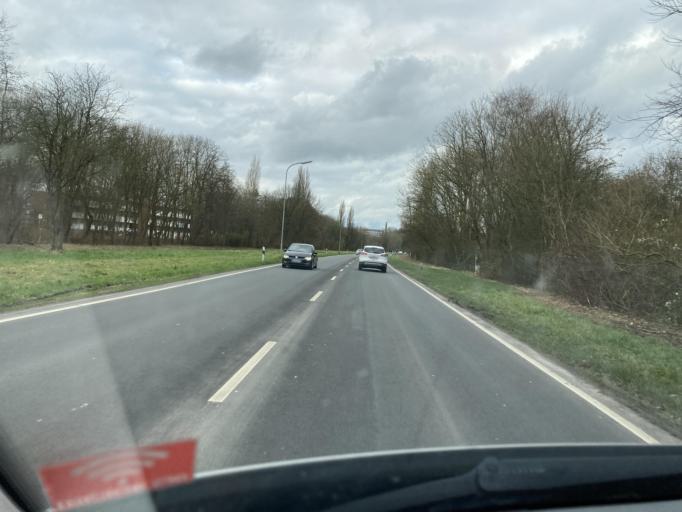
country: DE
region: Lower Saxony
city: Wilhelmshaven
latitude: 53.5370
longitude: 8.0893
